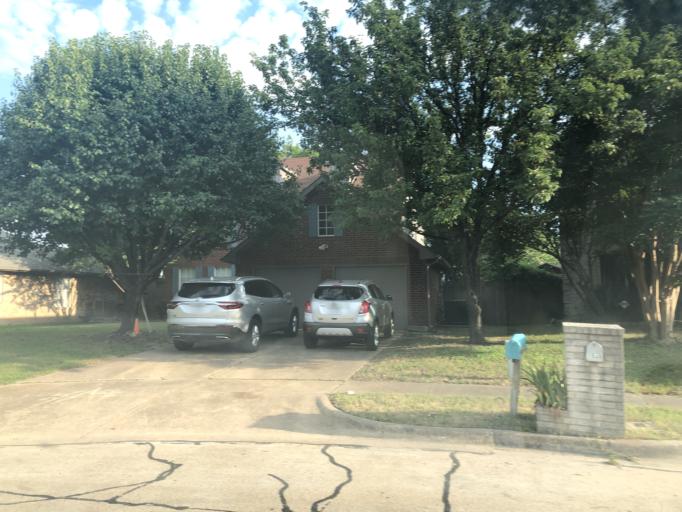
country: US
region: Texas
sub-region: Dallas County
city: Irving
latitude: 32.7903
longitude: -96.9673
